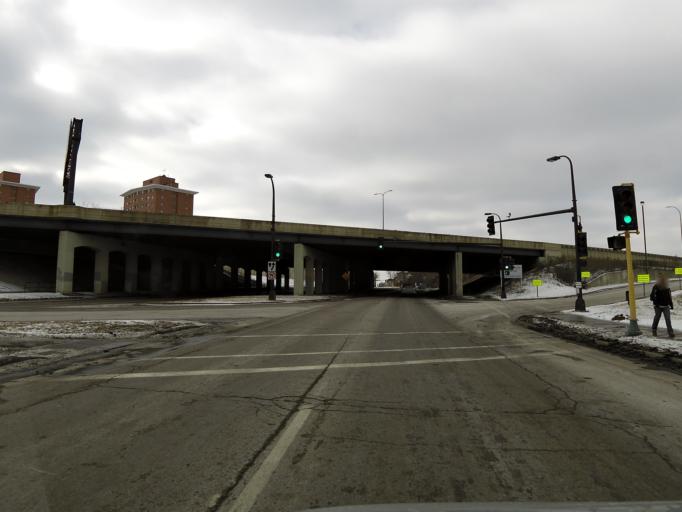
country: US
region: Minnesota
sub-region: Hennepin County
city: Minneapolis
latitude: 44.9625
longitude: -93.2483
